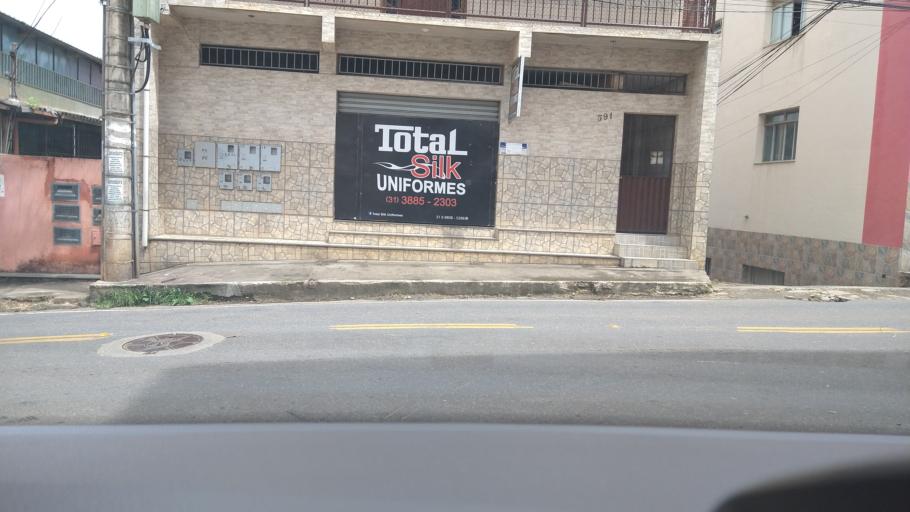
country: BR
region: Minas Gerais
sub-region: Vicosa
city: Vicosa
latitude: -20.7632
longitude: -42.8834
